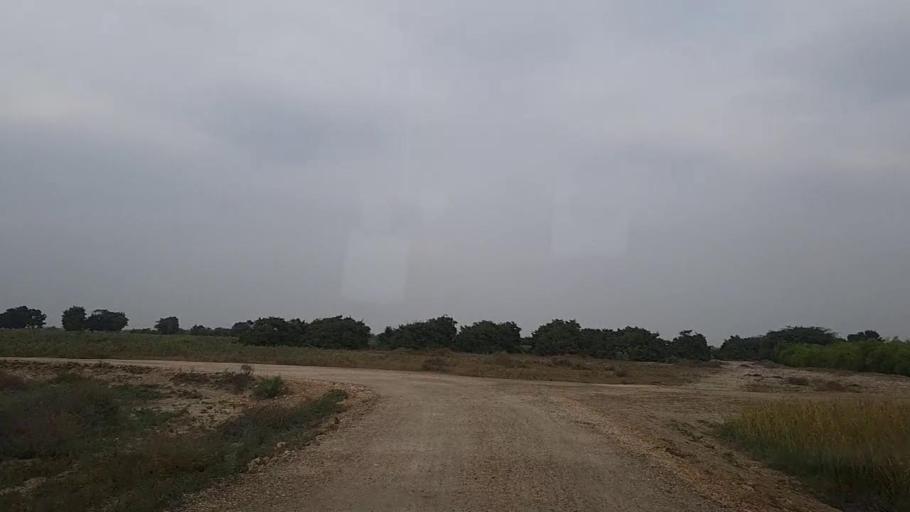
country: PK
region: Sindh
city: Mirpur Sakro
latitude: 24.6188
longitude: 67.7188
